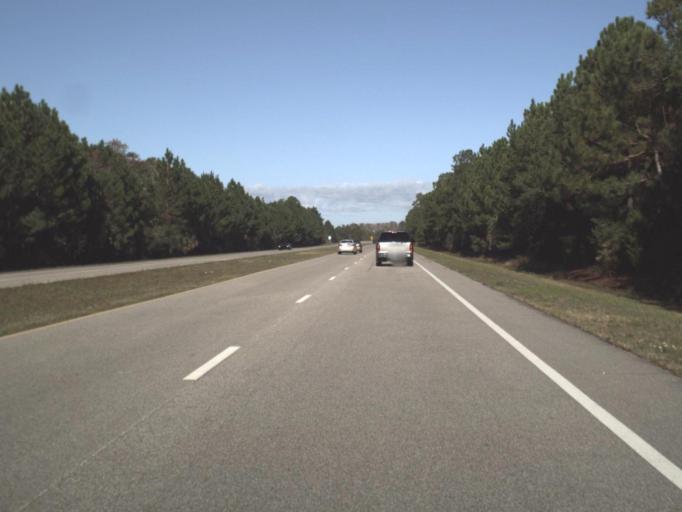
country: US
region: Florida
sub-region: Volusia County
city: Holly Hill
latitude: 29.2202
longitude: -81.0828
